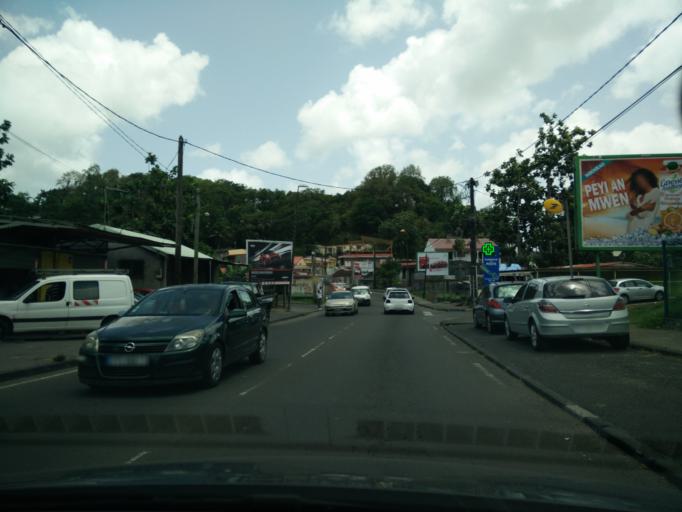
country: GP
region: Guadeloupe
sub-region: Guadeloupe
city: Les Abymes
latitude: 16.2741
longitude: -61.5044
